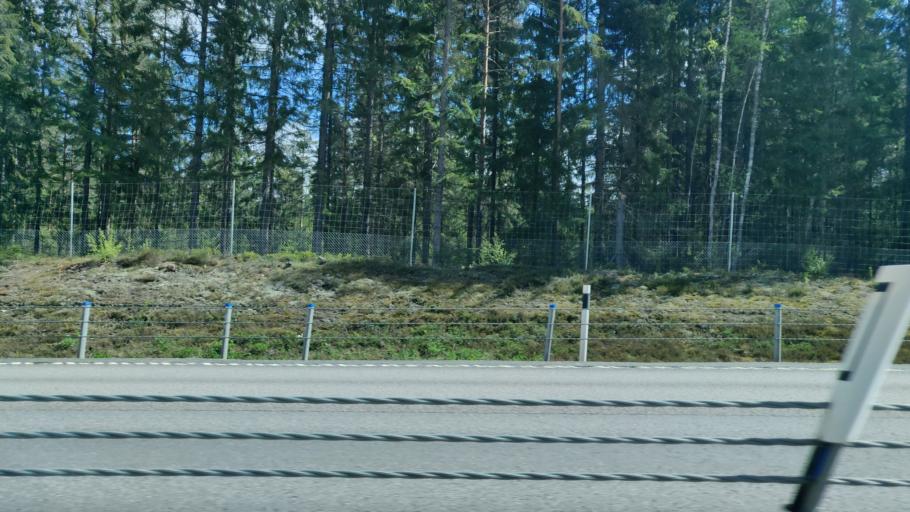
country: SE
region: Vaermland
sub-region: Karlstads Kommun
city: Karlstad
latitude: 59.4271
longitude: 13.5357
